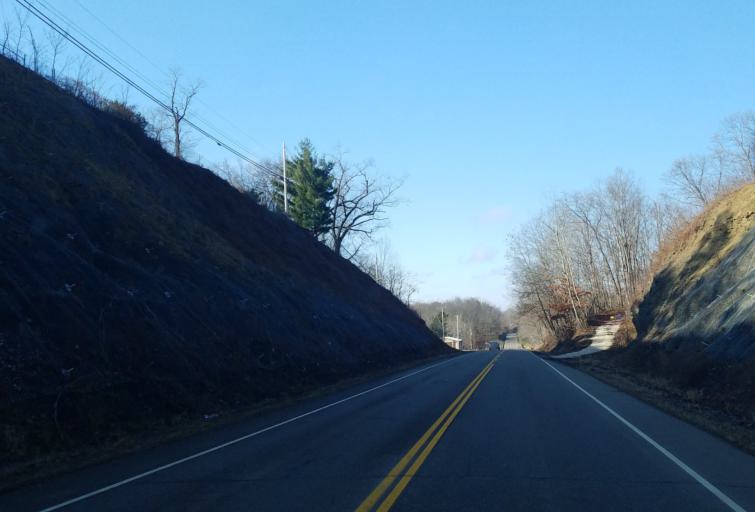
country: US
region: Ohio
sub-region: Guernsey County
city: Byesville
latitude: 40.0366
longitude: -81.4792
